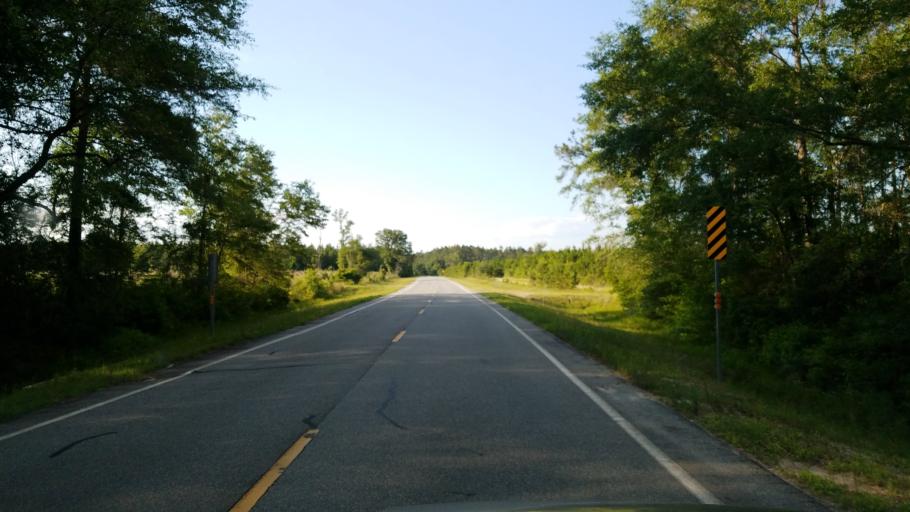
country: US
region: Georgia
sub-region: Echols County
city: Statenville
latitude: 30.8392
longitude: -83.0537
